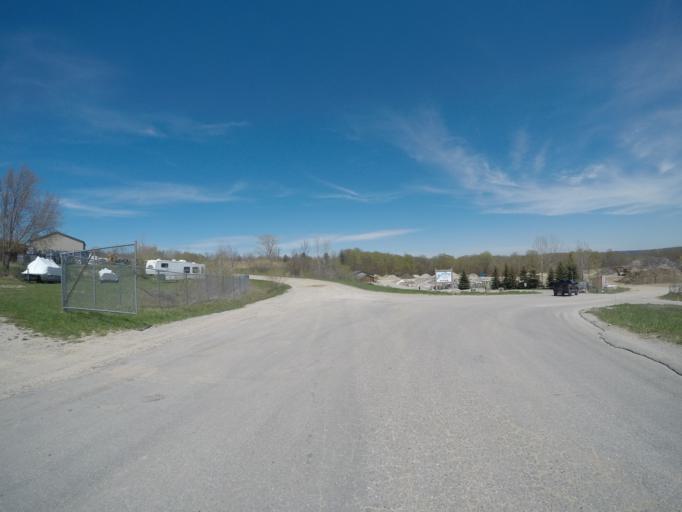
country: US
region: Michigan
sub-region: Grand Traverse County
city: Traverse City
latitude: 44.6957
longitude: -85.6516
